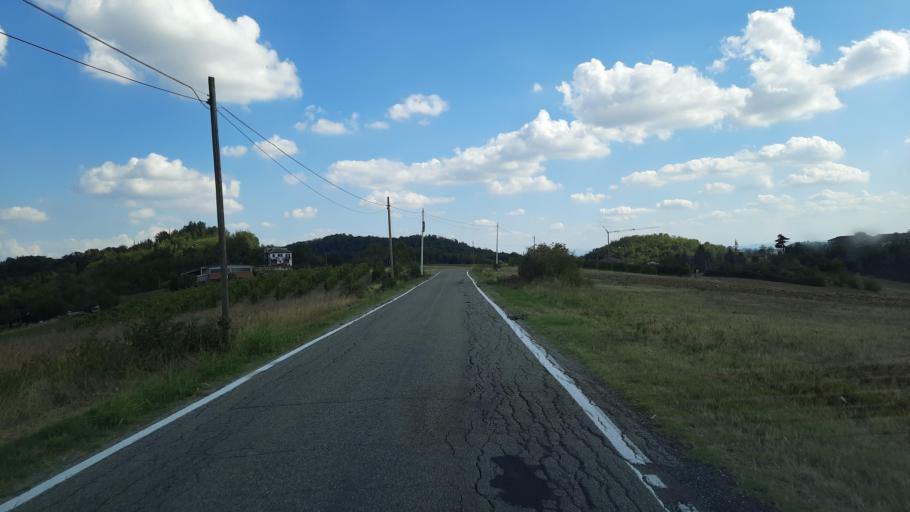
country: IT
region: Piedmont
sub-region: Provincia di Alessandria
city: Ottiglio
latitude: 45.0620
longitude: 8.3401
